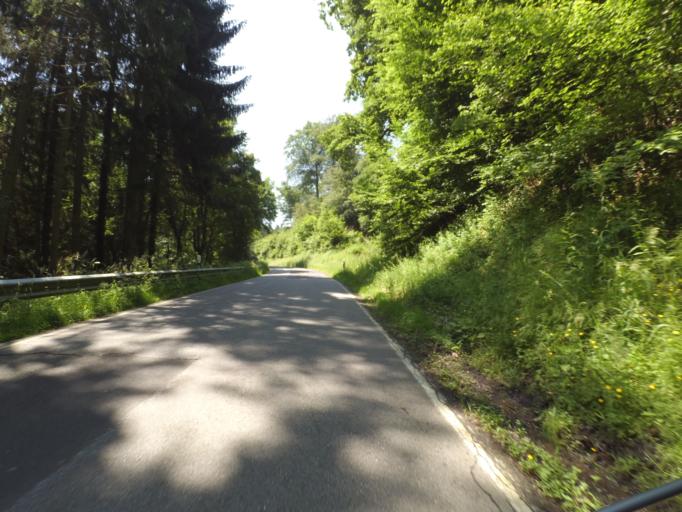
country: DE
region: Rheinland-Pfalz
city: Utzenhain
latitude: 50.1418
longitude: 7.6398
